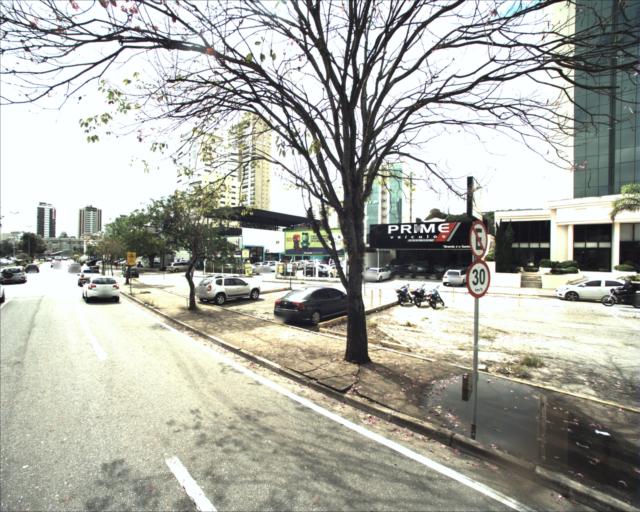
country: BR
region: Sao Paulo
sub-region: Sorocaba
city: Sorocaba
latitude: -23.5208
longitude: -47.4647
